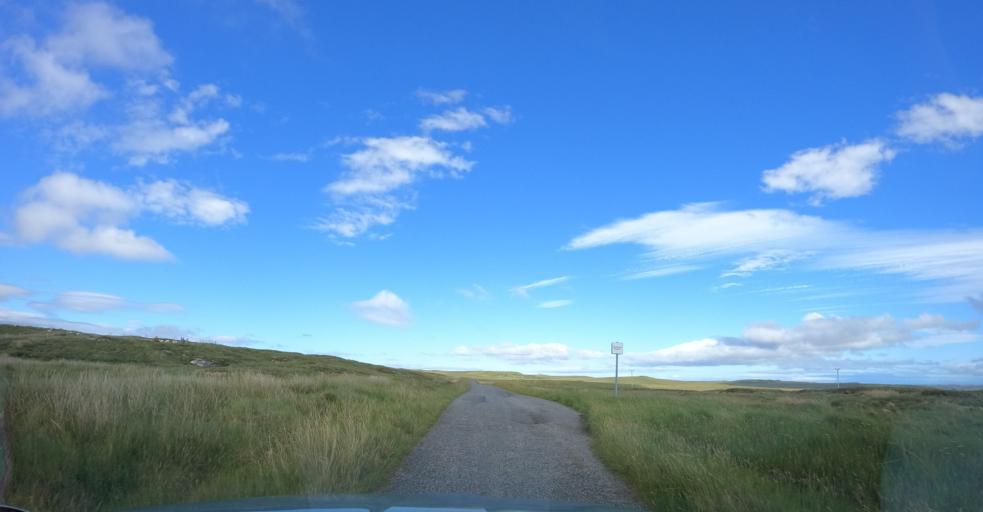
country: GB
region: Scotland
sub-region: Eilean Siar
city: Stornoway
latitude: 58.1734
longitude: -6.5619
